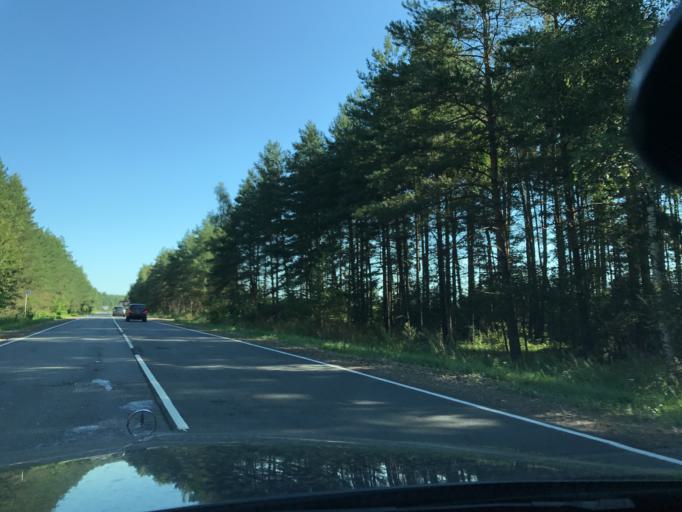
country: RU
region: Moskovskaya
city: Noginsk-9
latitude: 56.0954
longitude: 38.5818
